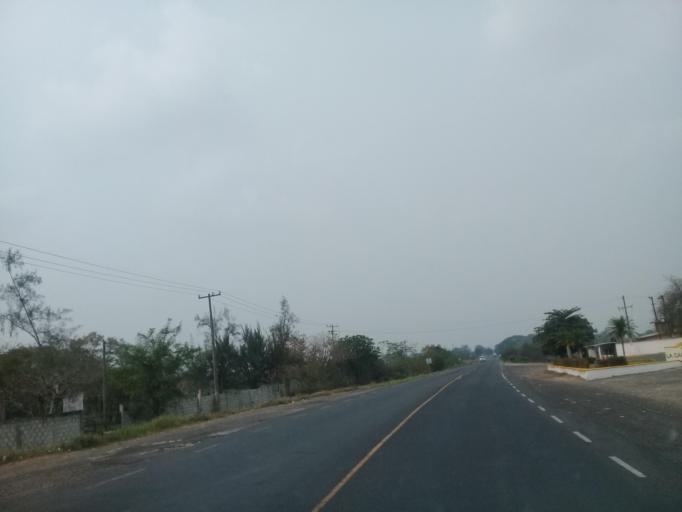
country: MX
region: Veracruz
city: Jamapa
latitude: 18.9169
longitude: -96.1972
